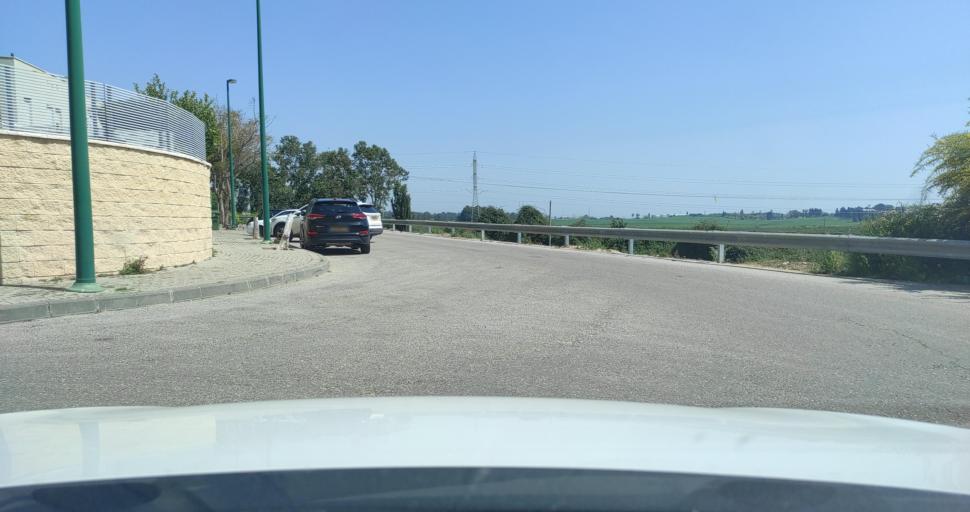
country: IL
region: Central District
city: Nordiyya
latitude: 32.2957
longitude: 34.8773
